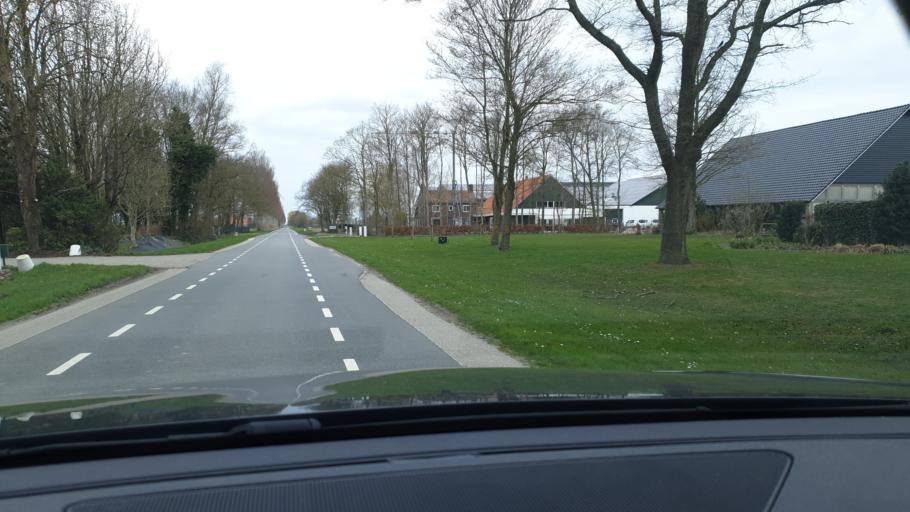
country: NL
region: Flevoland
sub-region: Gemeente Urk
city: Urk
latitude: 52.7252
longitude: 5.6327
